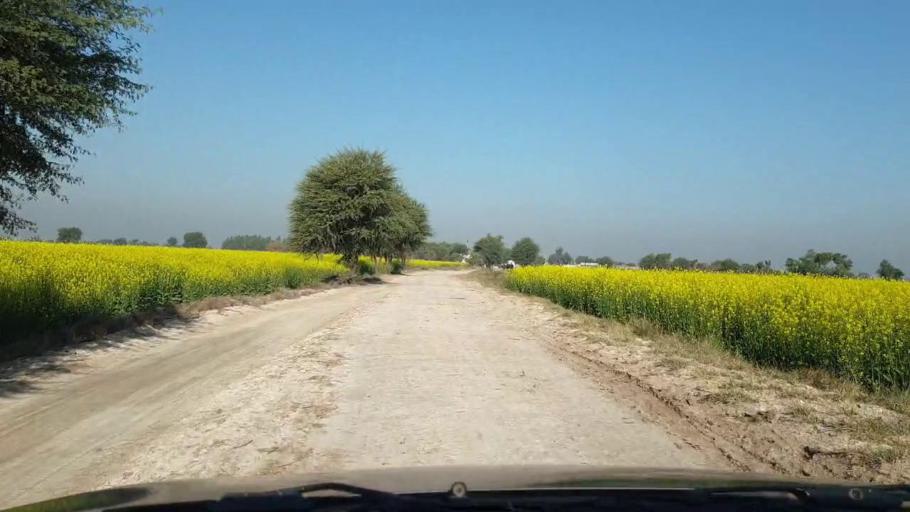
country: PK
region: Sindh
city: Jhol
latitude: 25.9371
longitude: 68.8418
